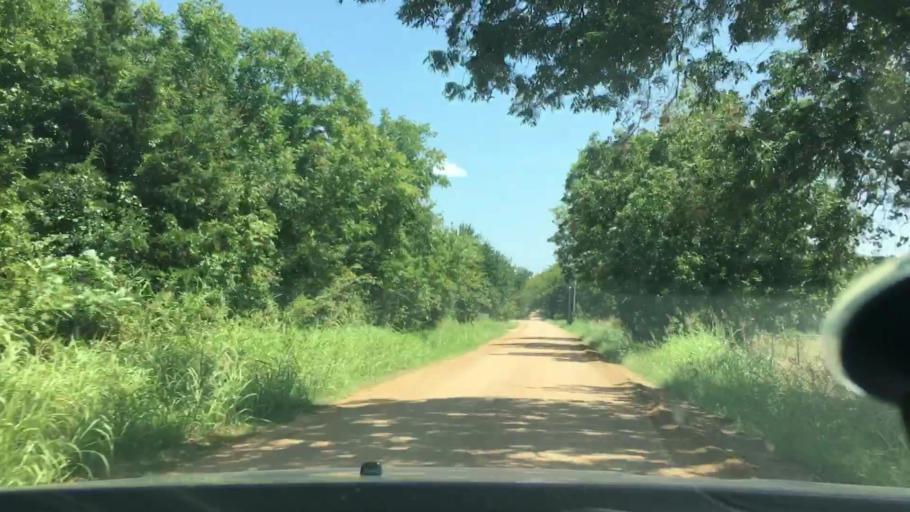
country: US
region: Oklahoma
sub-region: Coal County
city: Coalgate
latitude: 34.3681
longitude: -96.4306
